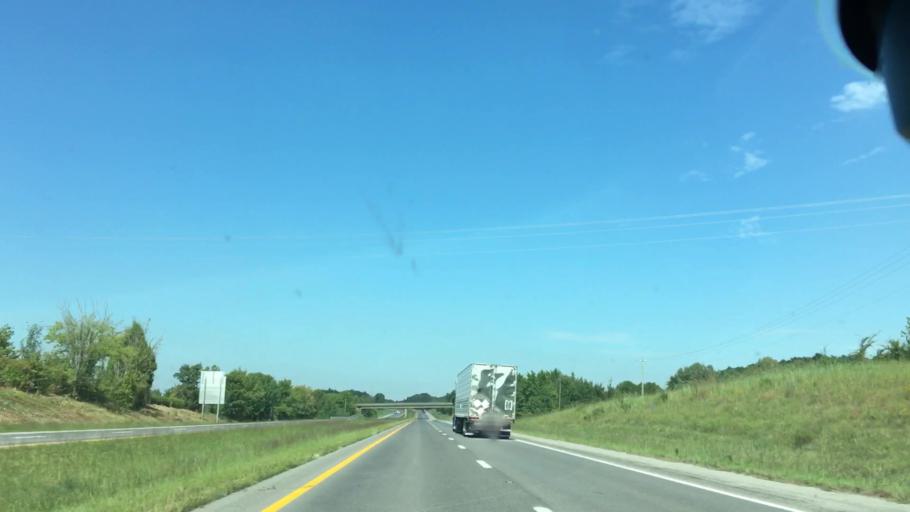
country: US
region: Kentucky
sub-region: Webster County
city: Sebree
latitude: 37.5056
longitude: -87.4750
